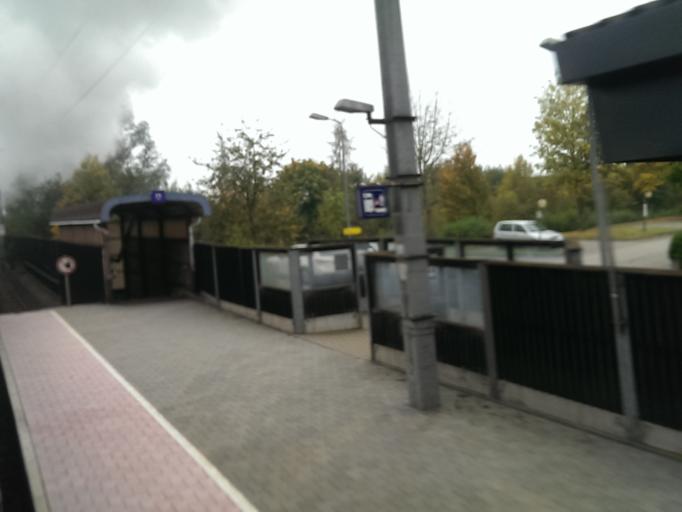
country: AT
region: Upper Austria
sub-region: Politischer Bezirk Linz-Land
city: Horsching
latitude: 48.2278
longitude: 14.1515
